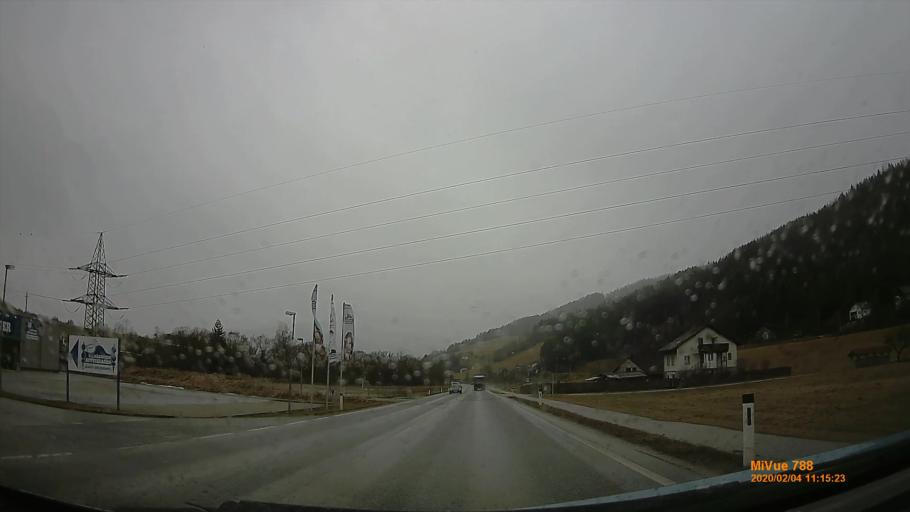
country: AT
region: Styria
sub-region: Politischer Bezirk Bruck-Muerzzuschlag
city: Muerzzuschlag
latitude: 47.6029
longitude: 15.7174
